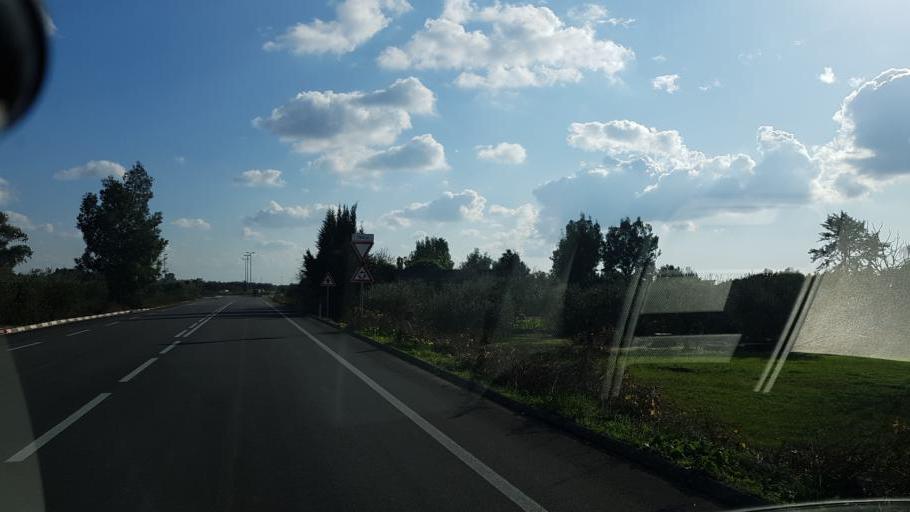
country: IT
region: Apulia
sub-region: Provincia di Lecce
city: Veglie
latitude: 40.3405
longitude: 17.9790
